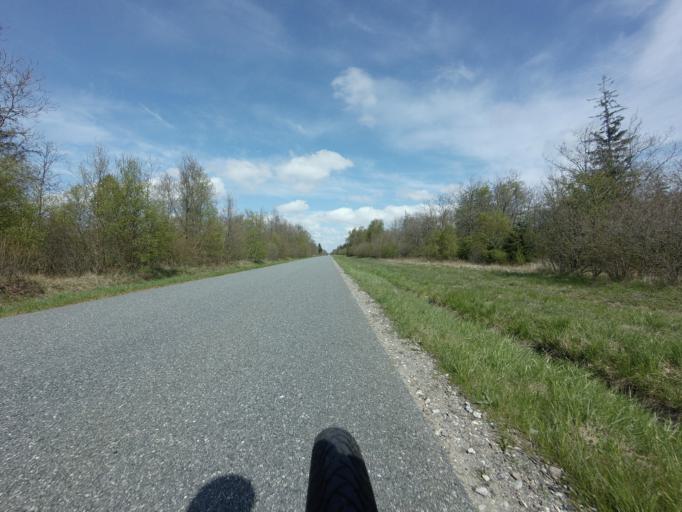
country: DK
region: North Denmark
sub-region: Jammerbugt Kommune
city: Brovst
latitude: 57.1662
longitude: 9.5432
